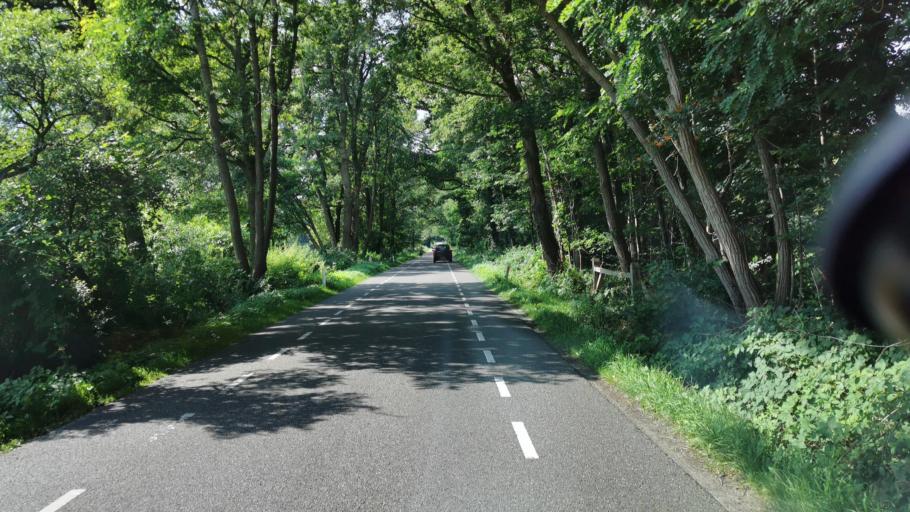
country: NL
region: Overijssel
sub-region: Gemeente Enschede
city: Enschede
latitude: 52.2264
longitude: 6.9372
